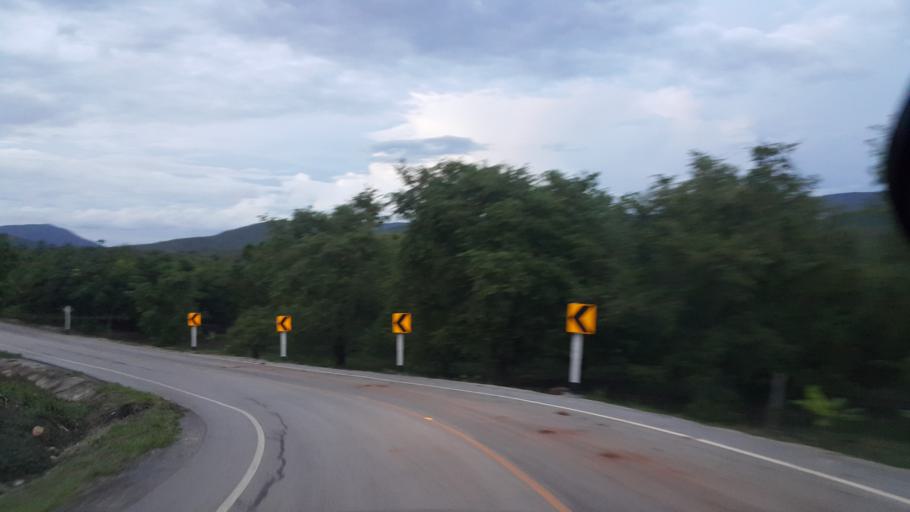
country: TH
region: Loei
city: Phu Ruea
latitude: 17.5160
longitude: 101.2327
